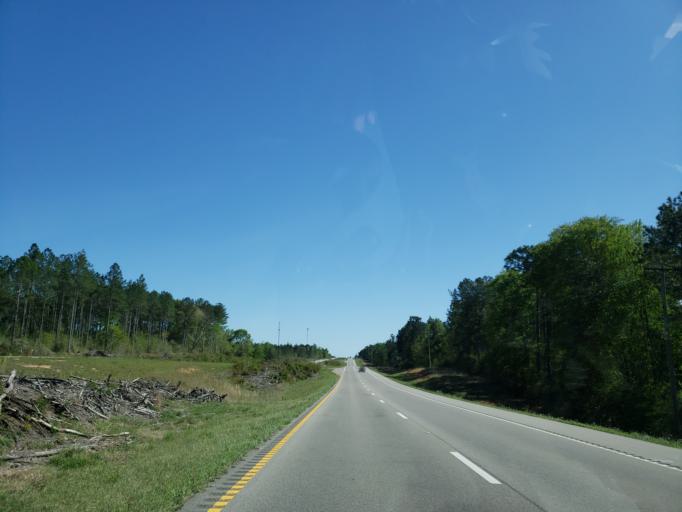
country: US
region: Mississippi
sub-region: Stone County
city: Wiggins
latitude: 30.9665
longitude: -89.1946
